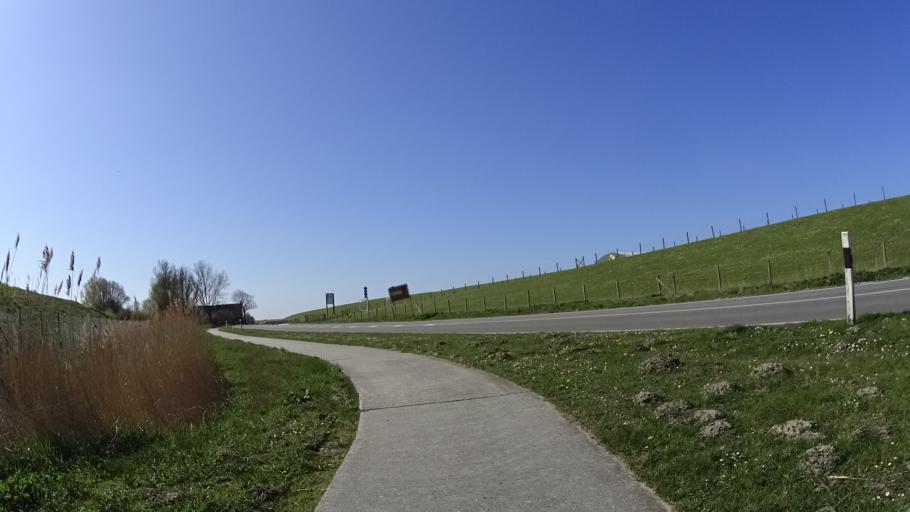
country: DE
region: Lower Saxony
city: Jemgum
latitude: 53.2651
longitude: 7.4075
